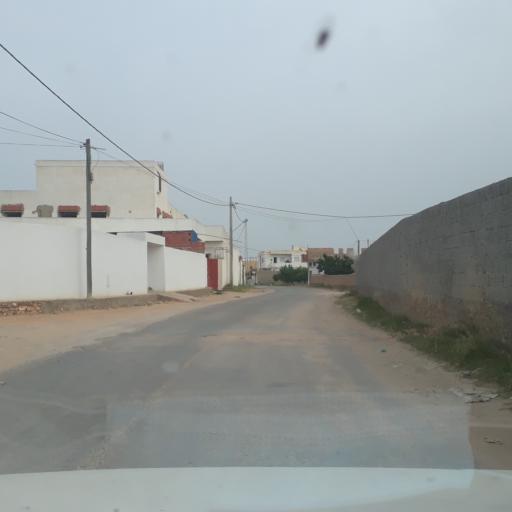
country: TN
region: Safaqis
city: Al Qarmadah
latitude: 34.8225
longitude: 10.7716
